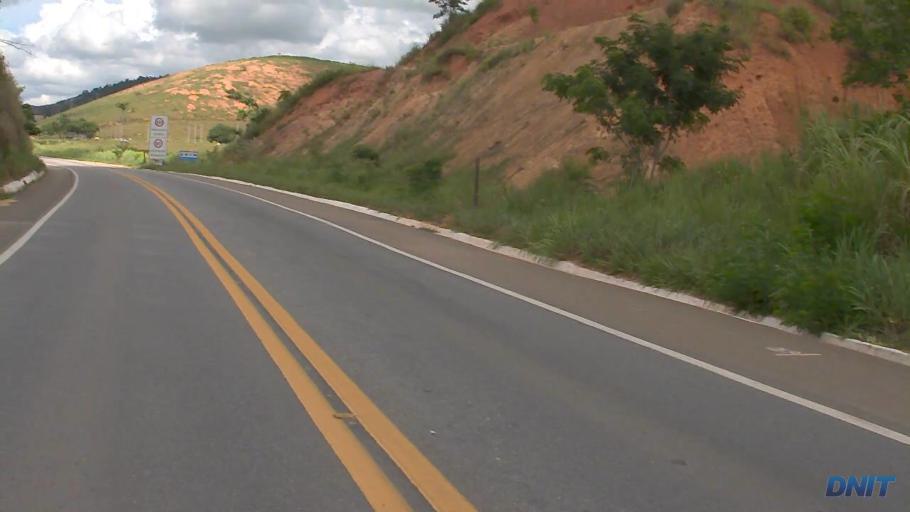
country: BR
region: Minas Gerais
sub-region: Governador Valadares
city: Governador Valadares
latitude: -18.9425
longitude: -42.0603
